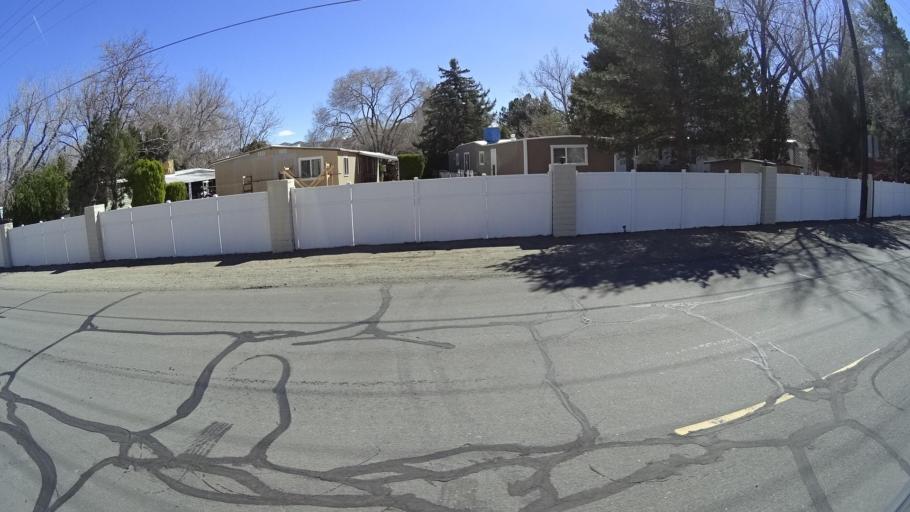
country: US
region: Nevada
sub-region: Washoe County
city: Sparks
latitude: 39.4816
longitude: -119.7607
